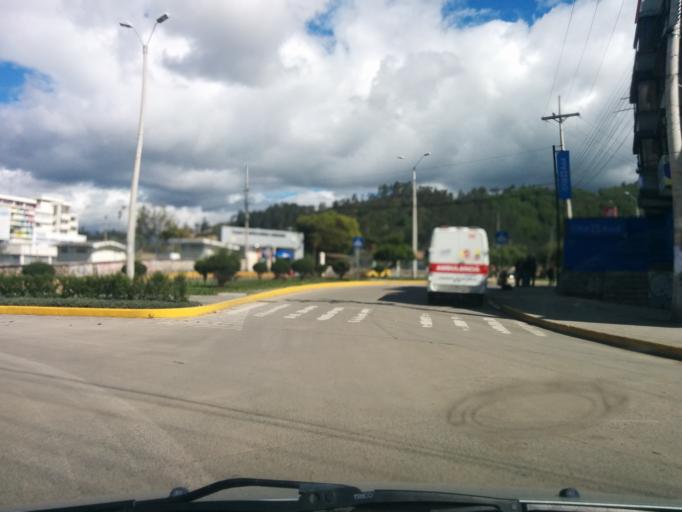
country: EC
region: Azuay
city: Cuenca
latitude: -2.9100
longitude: -78.9941
